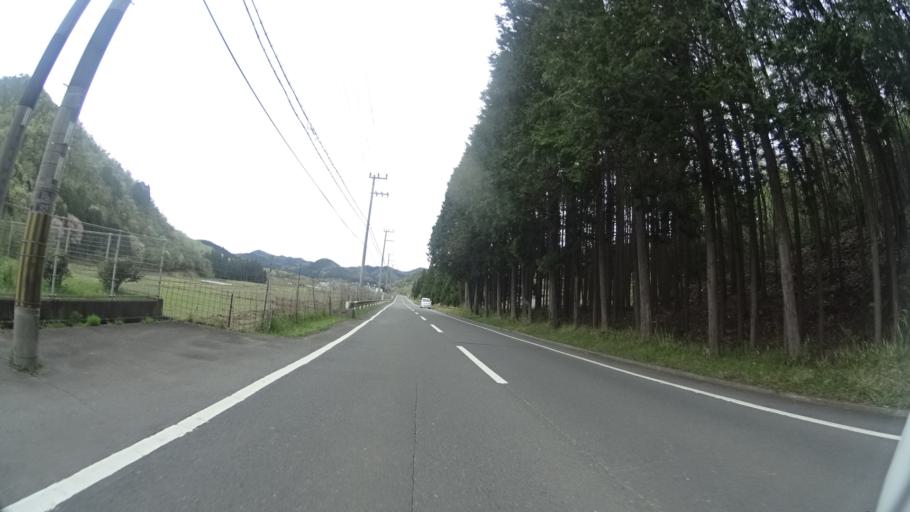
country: JP
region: Kyoto
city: Ayabe
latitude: 35.1825
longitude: 135.4335
